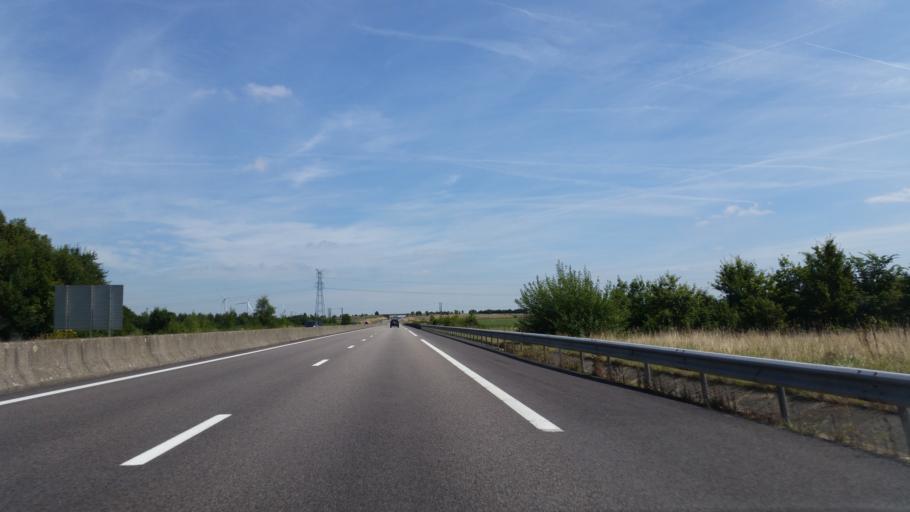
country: FR
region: Haute-Normandie
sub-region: Departement de la Seine-Maritime
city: Aumale
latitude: 49.7907
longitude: 1.7821
